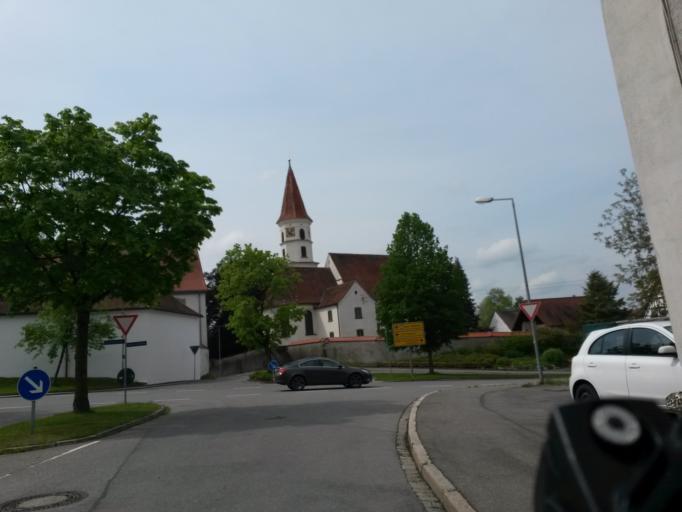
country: DE
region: Baden-Wuerttemberg
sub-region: Tuebingen Region
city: Bad Waldsee
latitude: 47.9650
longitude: 9.7269
